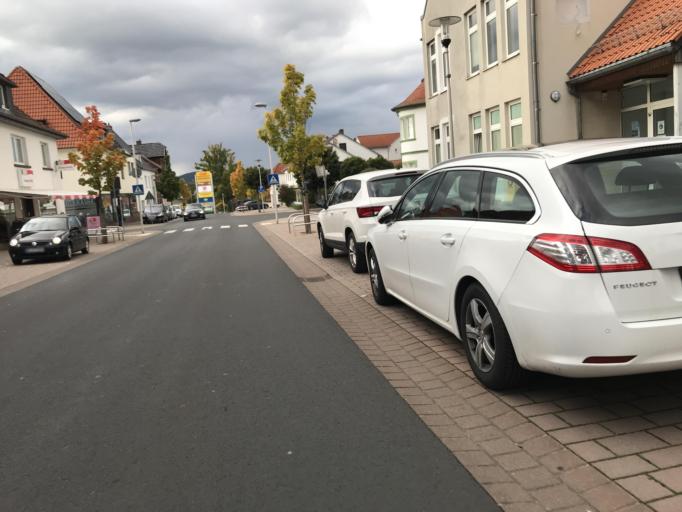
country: DE
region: Hesse
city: Borken
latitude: 51.0480
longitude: 9.2785
